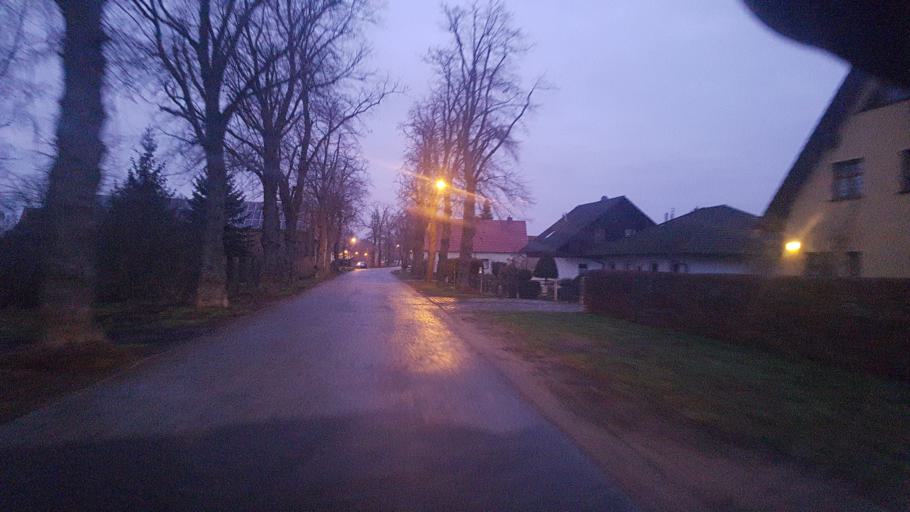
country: DE
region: Brandenburg
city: Luckenwalde
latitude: 52.1048
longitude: 13.1066
